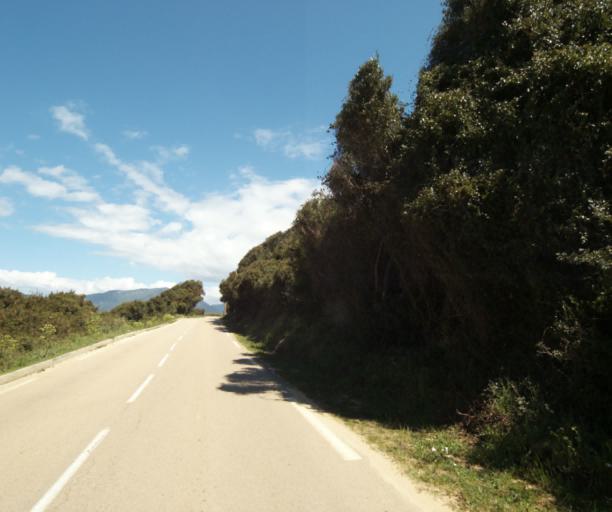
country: FR
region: Corsica
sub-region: Departement de la Corse-du-Sud
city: Propriano
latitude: 41.6500
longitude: 8.8798
